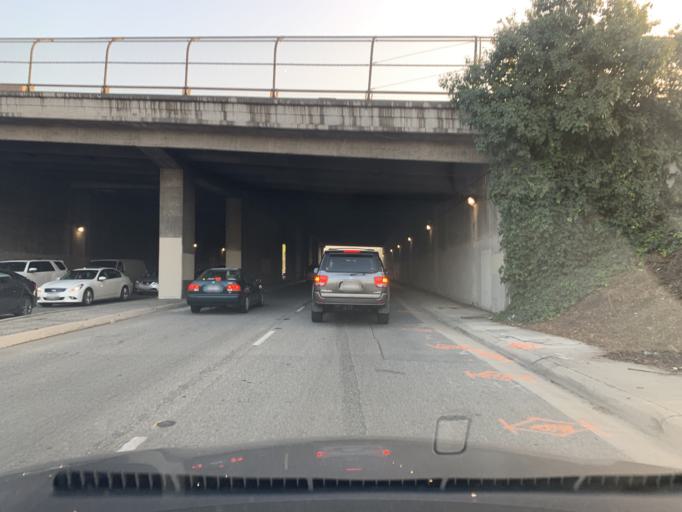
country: US
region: California
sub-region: Los Angeles County
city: Covina
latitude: 34.0724
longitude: -117.8725
